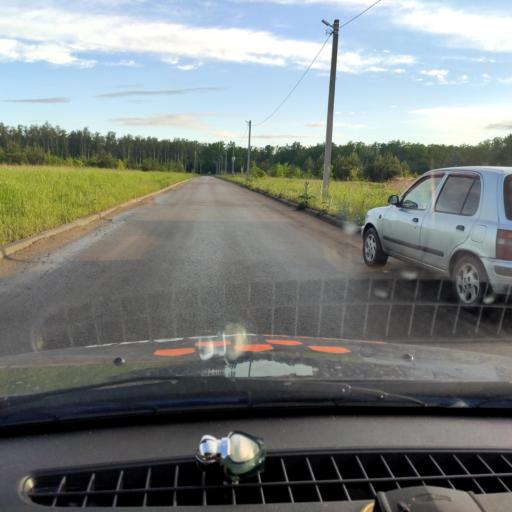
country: RU
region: Voronezj
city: Podgornoye
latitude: 51.7879
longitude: 39.1902
